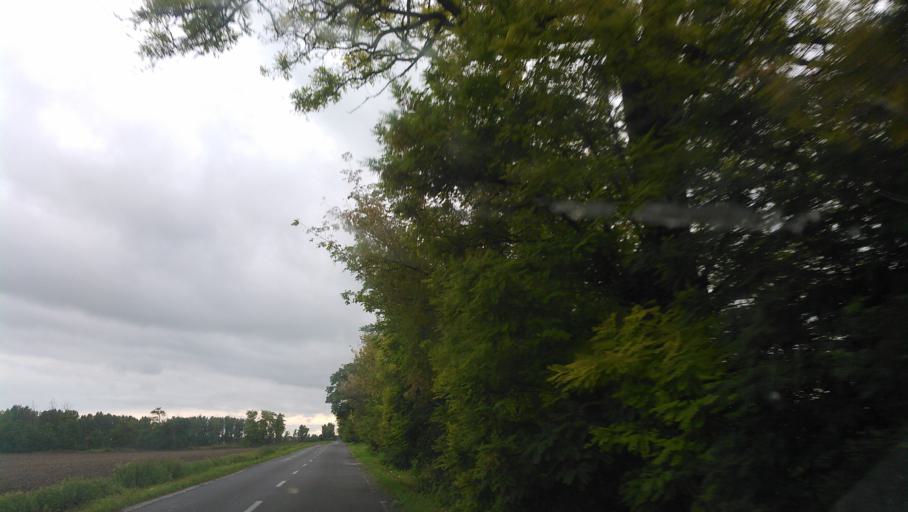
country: SK
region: Trnavsky
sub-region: Okres Dunajska Streda
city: Velky Meder
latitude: 47.9184
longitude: 17.7459
